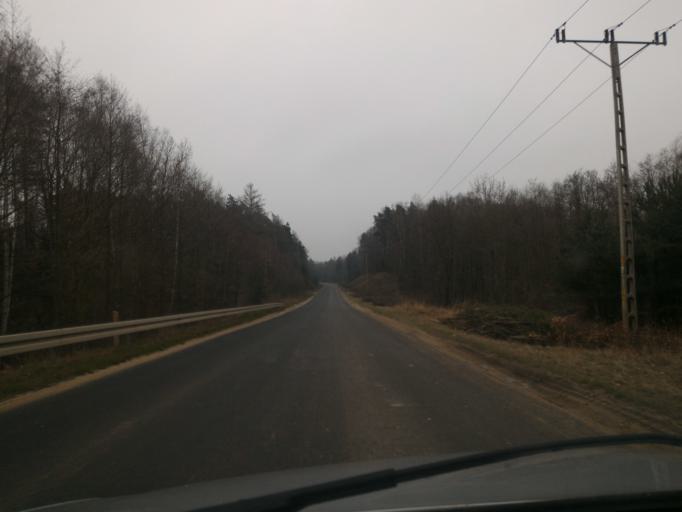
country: CZ
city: Hradek nad Nisou
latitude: 50.8821
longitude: 14.8846
